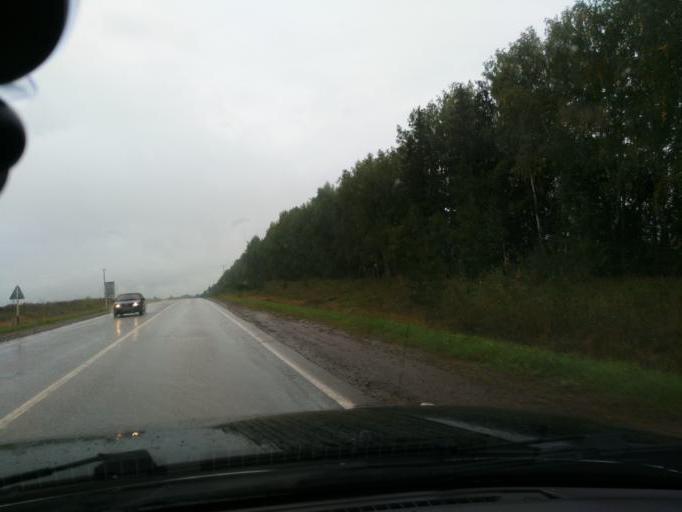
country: RU
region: Perm
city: Osa
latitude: 57.3767
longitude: 55.6096
